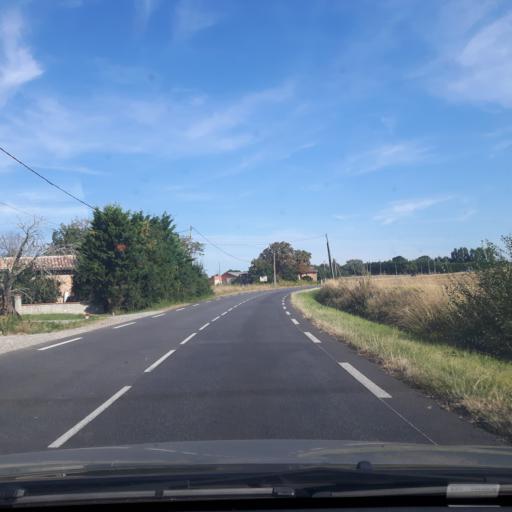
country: FR
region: Midi-Pyrenees
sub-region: Departement de la Haute-Garonne
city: Villeneuve-les-Bouloc
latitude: 43.7683
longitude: 1.4392
